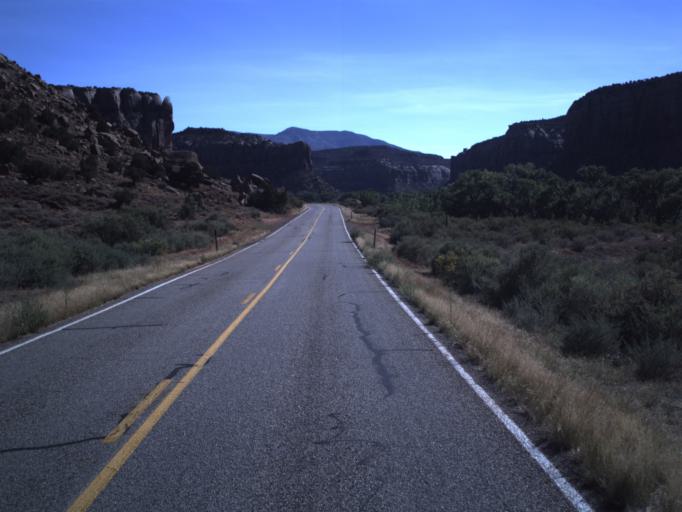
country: US
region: Utah
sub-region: San Juan County
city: Monticello
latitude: 38.0504
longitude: -109.5528
